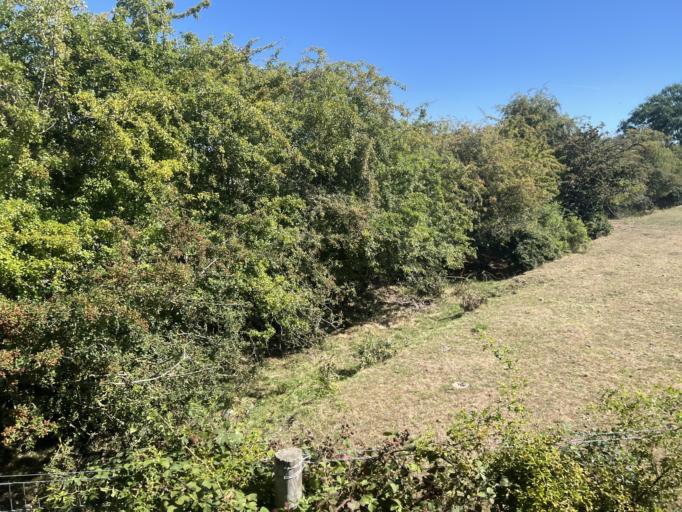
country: GB
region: England
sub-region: Lincolnshire
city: Wainfleet All Saints
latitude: 53.1217
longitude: 0.2013
